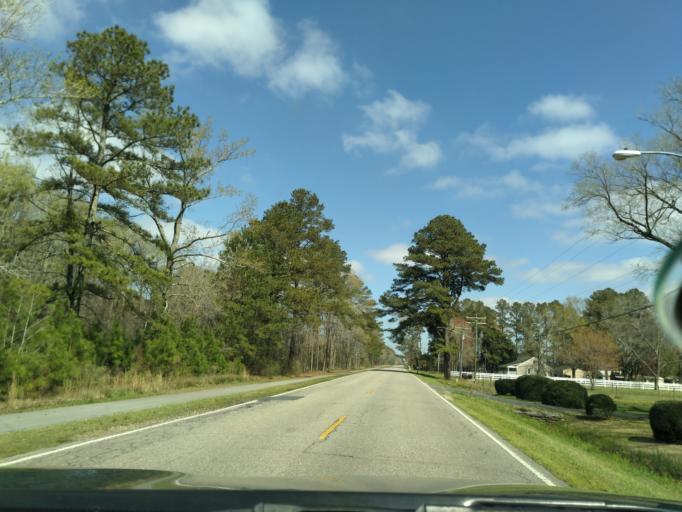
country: US
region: Virginia
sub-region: City of Portsmouth
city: Portsmouth Heights
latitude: 36.7155
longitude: -76.3519
